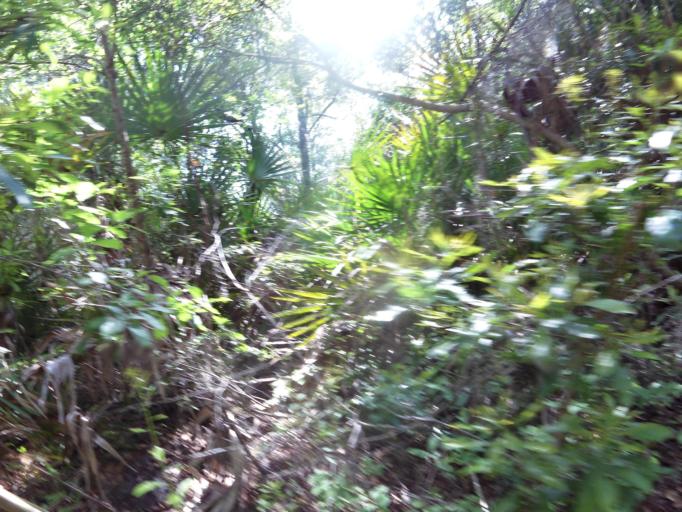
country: US
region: Florida
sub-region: Nassau County
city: Yulee
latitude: 30.4881
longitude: -81.5005
